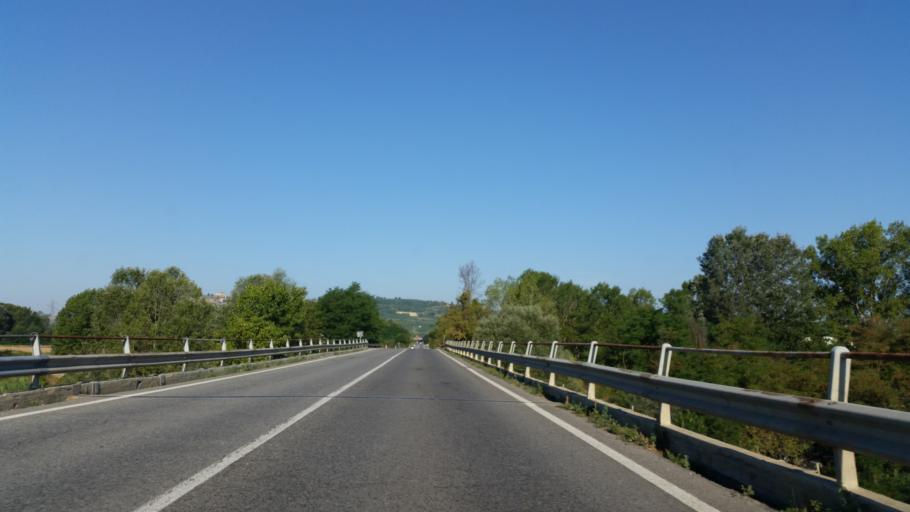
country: IT
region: Piedmont
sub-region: Provincia di Cuneo
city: Barbaresco
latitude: 44.7415
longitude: 8.0881
